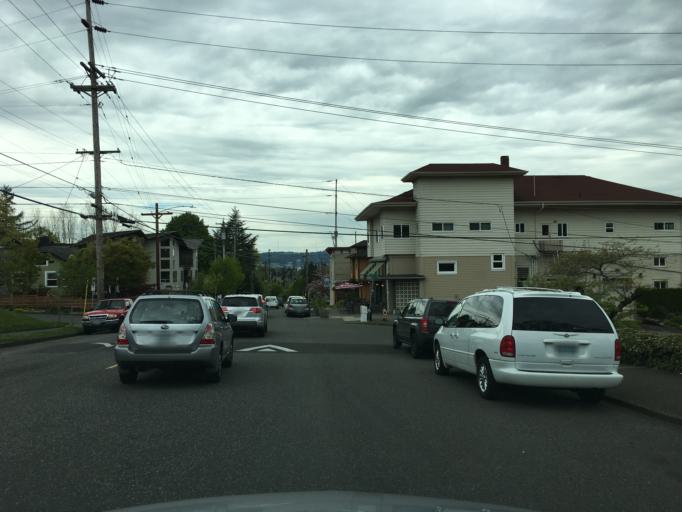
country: US
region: Oregon
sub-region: Multnomah County
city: Lents
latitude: 45.5193
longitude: -122.6008
